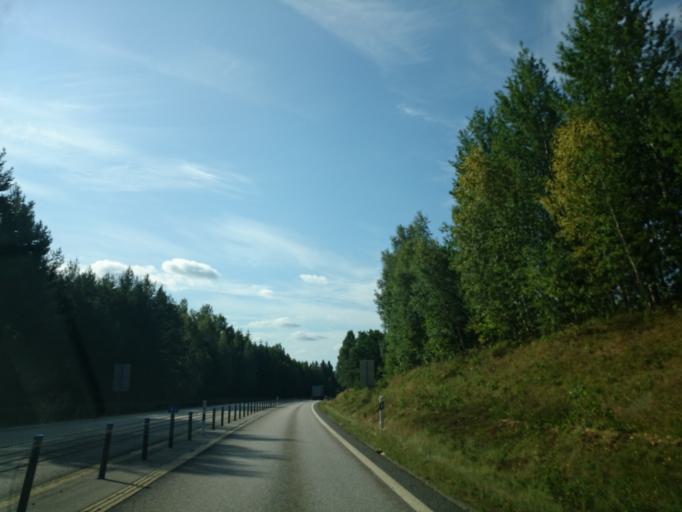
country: SE
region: OEstergoetland
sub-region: Valdemarsviks Kommun
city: Valdemarsvik
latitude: 58.1160
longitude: 16.5405
